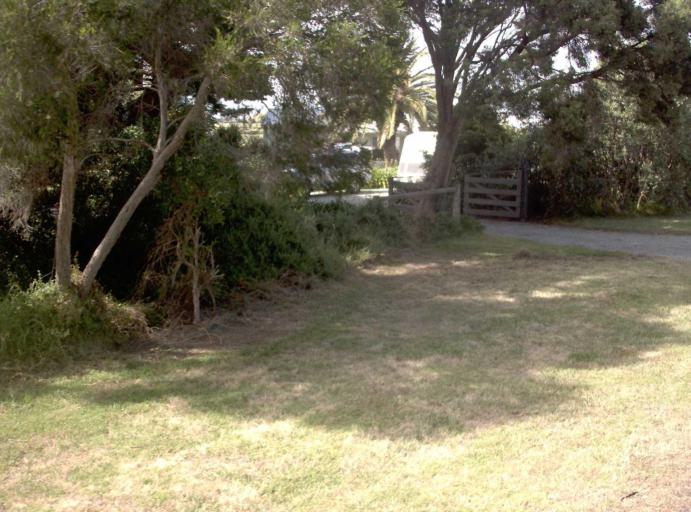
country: AU
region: Victoria
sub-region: Bass Coast
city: Phillip Island
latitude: -38.4915
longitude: 145.1656
